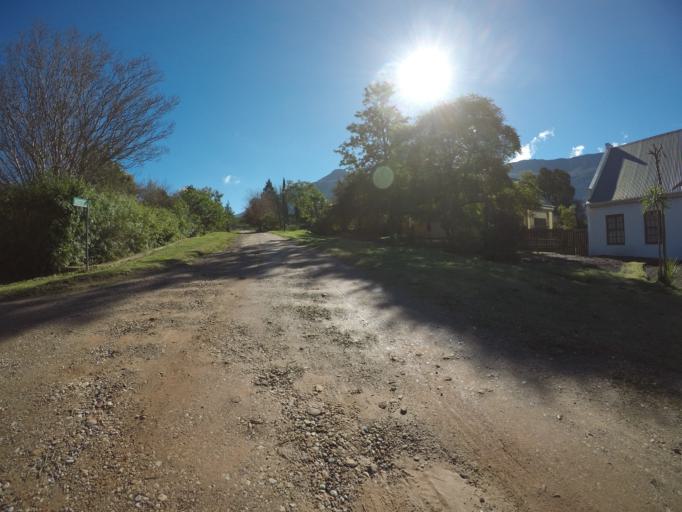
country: ZA
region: Western Cape
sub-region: Overberg District Municipality
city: Caledon
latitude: -34.0480
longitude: 19.6097
